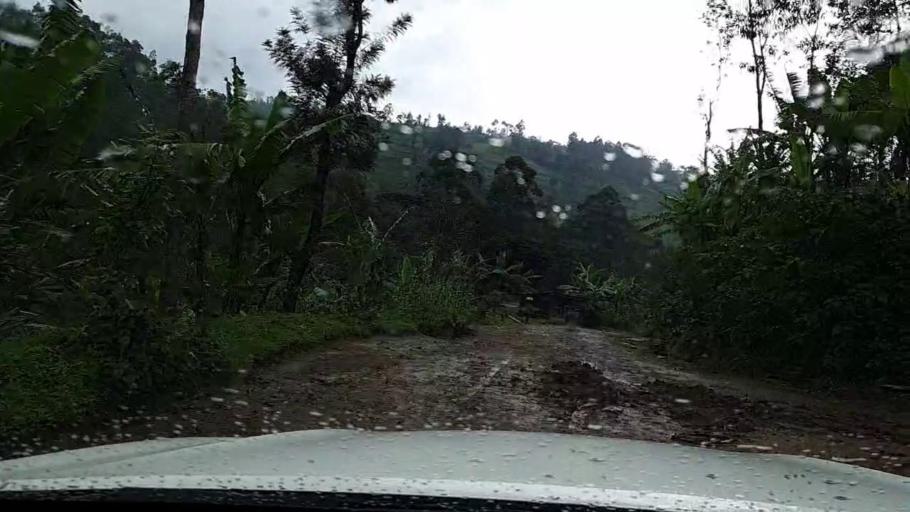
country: RW
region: Western Province
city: Cyangugu
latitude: -2.5342
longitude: 29.0421
